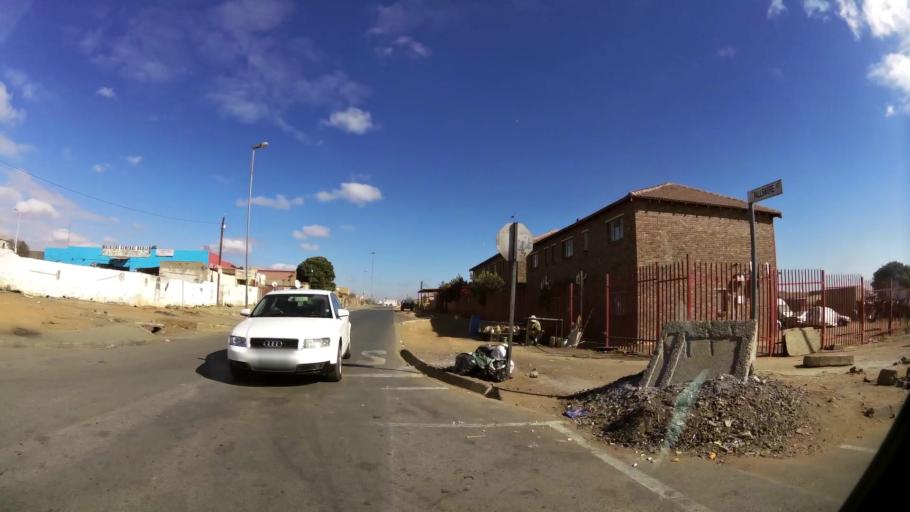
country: ZA
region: Gauteng
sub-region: City of Johannesburg Metropolitan Municipality
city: Modderfontein
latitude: -26.0446
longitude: 28.1781
